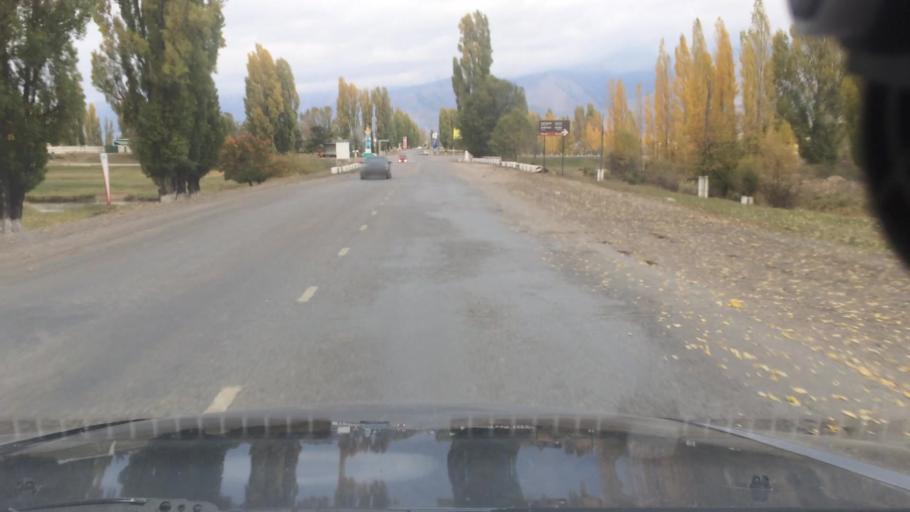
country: KG
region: Ysyk-Koel
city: Tyup
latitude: 42.7375
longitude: 78.3477
